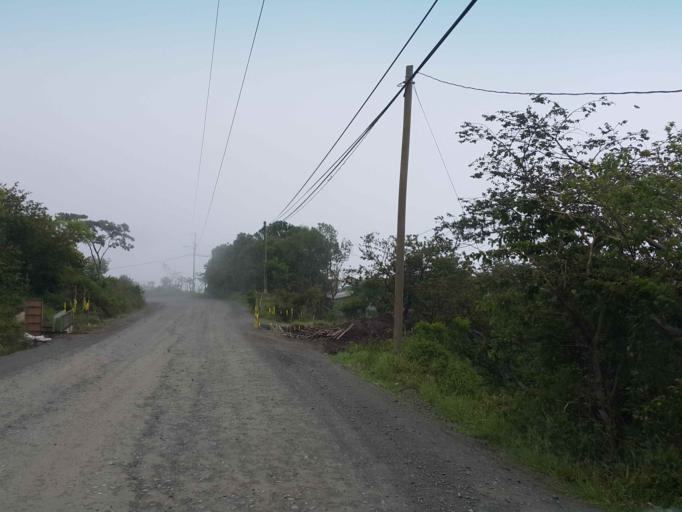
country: CR
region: Guanacaste
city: Juntas
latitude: 10.3021
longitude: -84.8363
